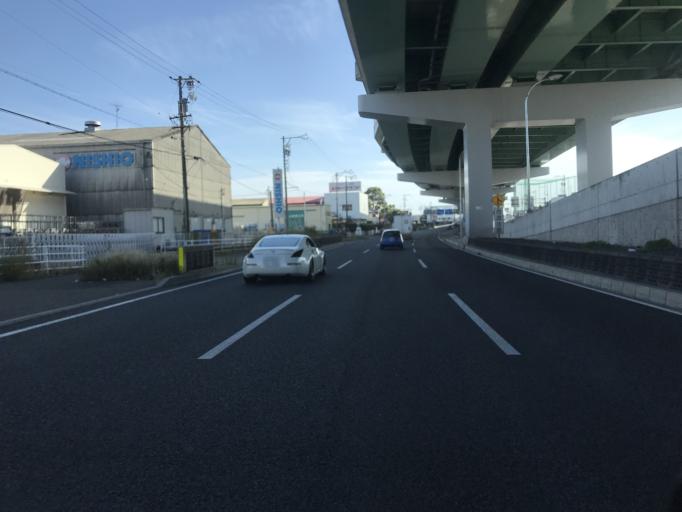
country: JP
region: Aichi
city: Iwakura
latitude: 35.2620
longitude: 136.8414
